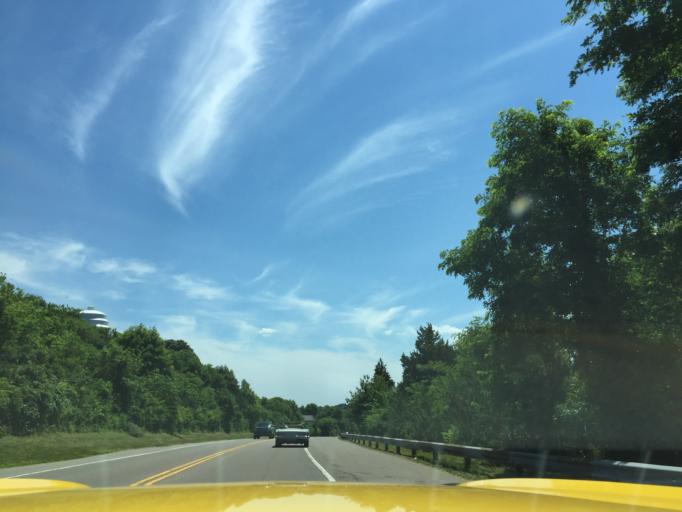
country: US
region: New York
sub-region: Suffolk County
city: Montauk
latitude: 41.0555
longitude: -71.9507
